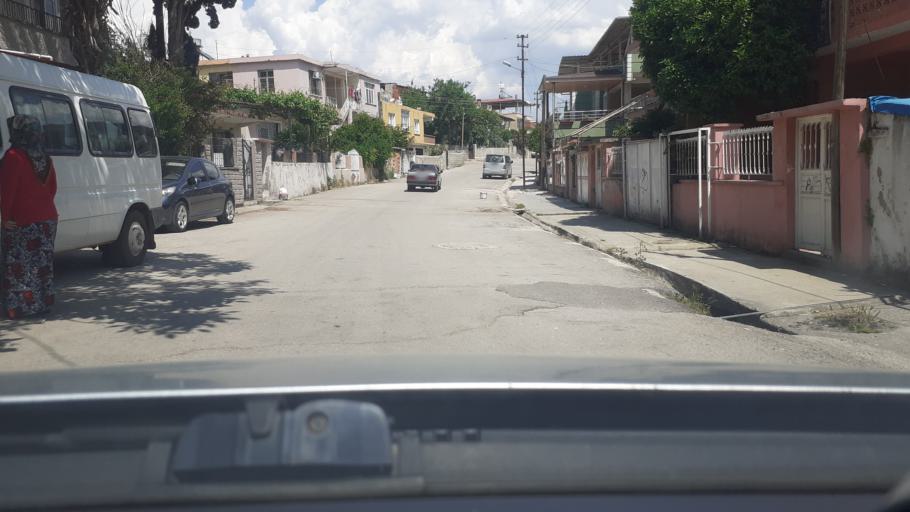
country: TR
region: Hatay
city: Kirikhan
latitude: 36.5021
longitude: 36.3548
